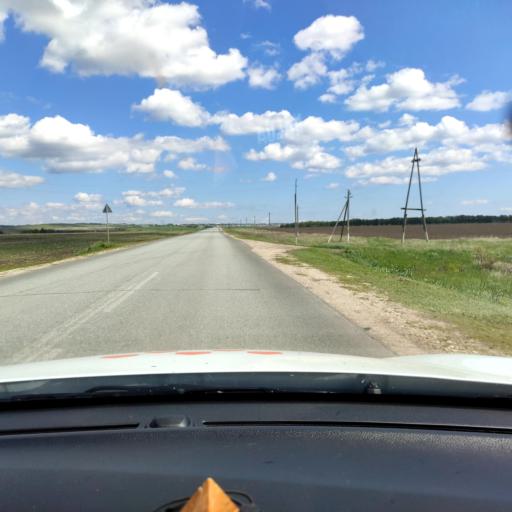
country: RU
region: Tatarstan
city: Kuybyshevskiy Zaton
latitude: 55.1632
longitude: 49.2001
